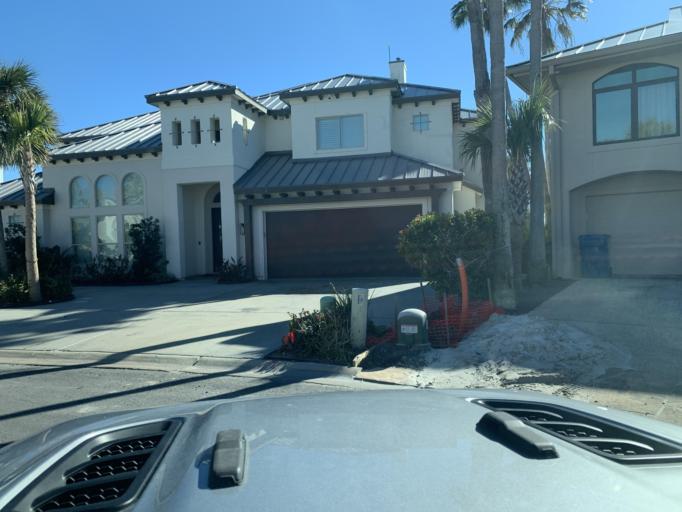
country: US
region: Texas
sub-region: Aransas County
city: Rockport
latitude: 28.0333
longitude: -97.0283
